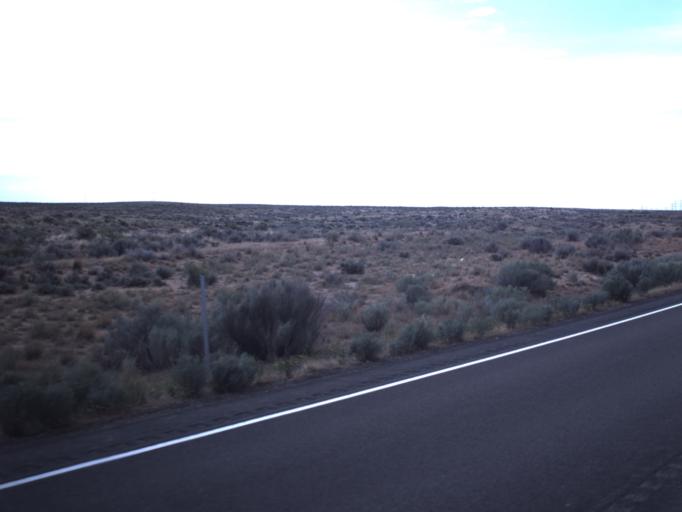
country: US
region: Utah
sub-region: Uintah County
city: Naples
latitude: 40.2321
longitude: -109.4110
